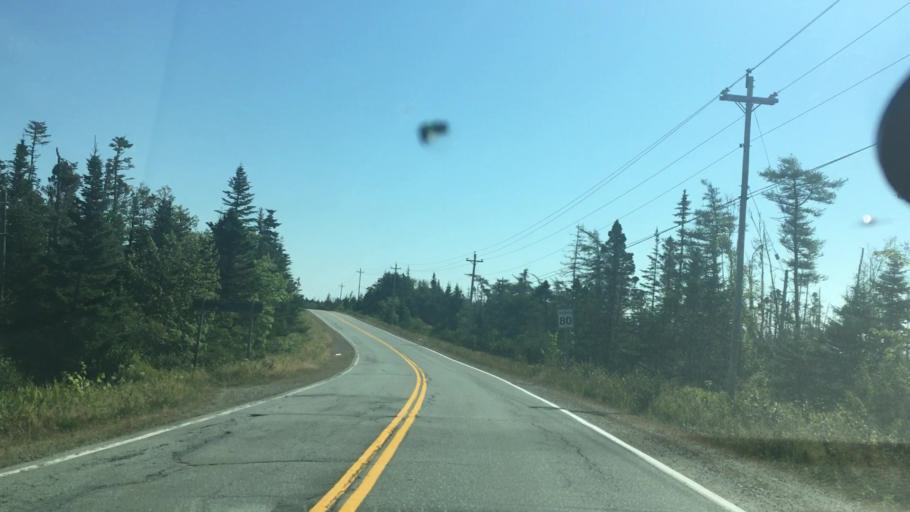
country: CA
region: Nova Scotia
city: New Glasgow
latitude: 44.9182
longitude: -62.3327
